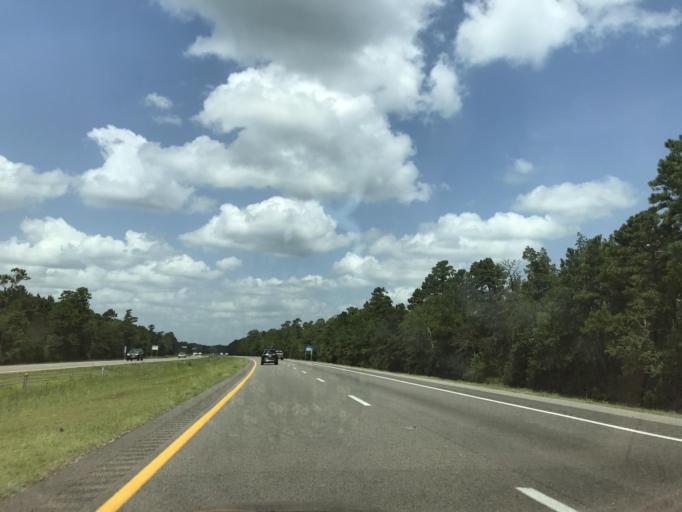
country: US
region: North Carolina
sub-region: Pender County
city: Burgaw
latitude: 34.5121
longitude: -77.8797
